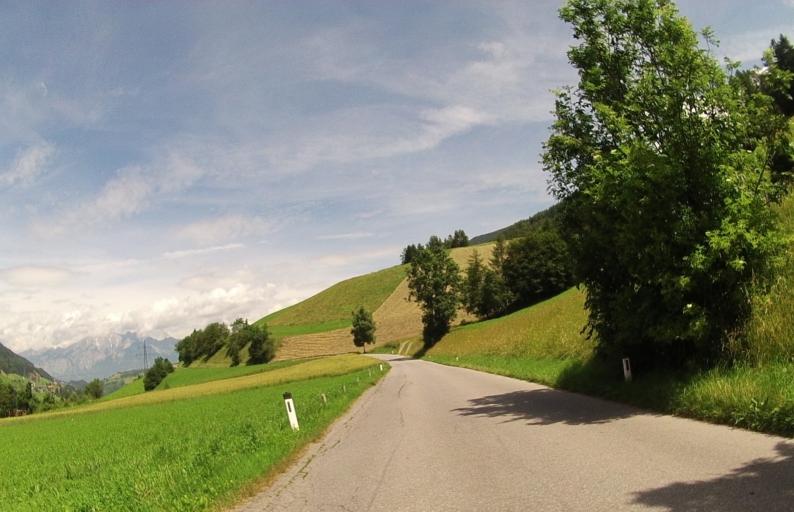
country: AT
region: Tyrol
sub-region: Politischer Bezirk Innsbruck Land
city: Pfons
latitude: 47.1465
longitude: 11.4569
